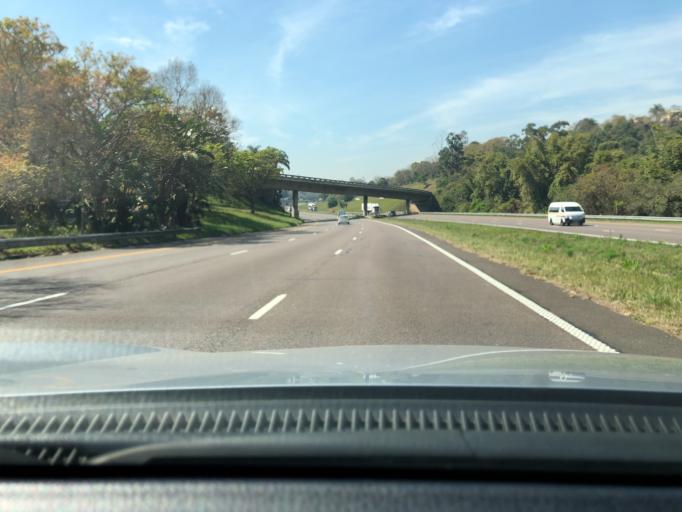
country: ZA
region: KwaZulu-Natal
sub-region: eThekwini Metropolitan Municipality
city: Berea
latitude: -29.8338
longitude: 30.8858
